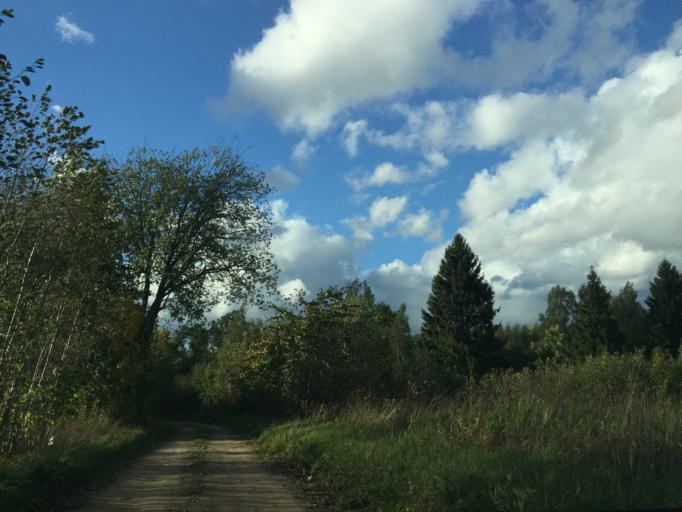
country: LV
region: Ligatne
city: Ligatne
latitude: 57.1245
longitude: 25.1297
